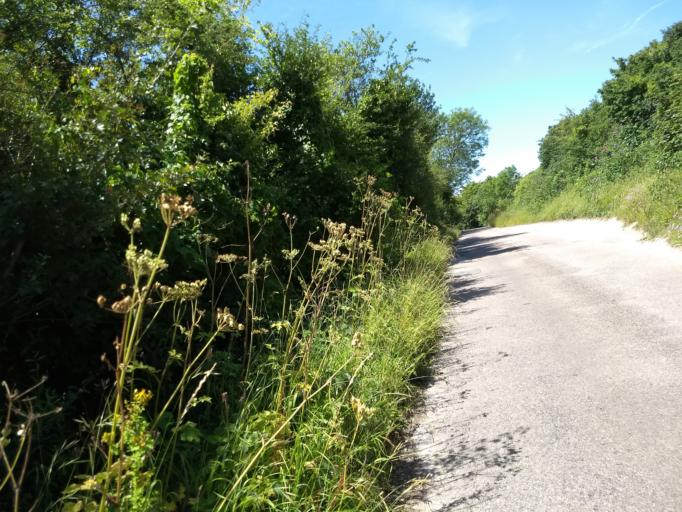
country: GB
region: England
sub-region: Isle of Wight
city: Brading
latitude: 50.6762
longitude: -1.1511
